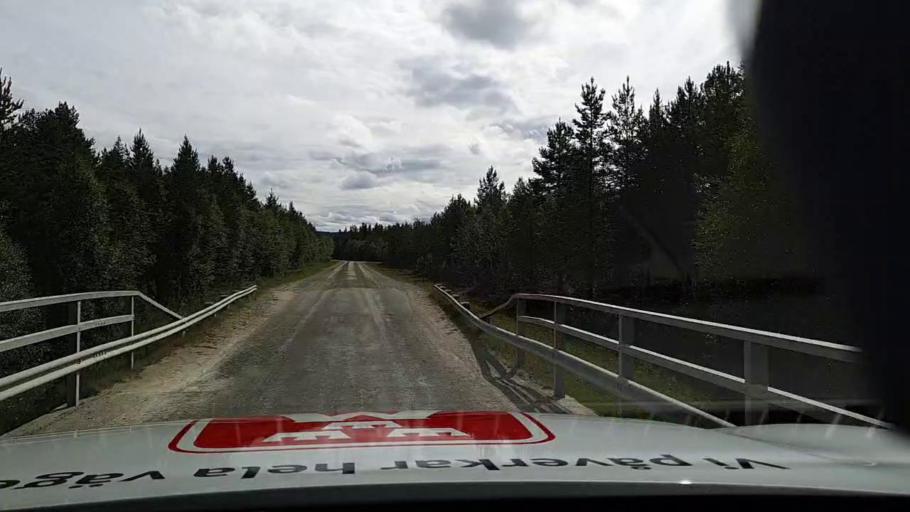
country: SE
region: Jaemtland
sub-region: Are Kommun
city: Jarpen
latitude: 62.5235
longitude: 13.4887
